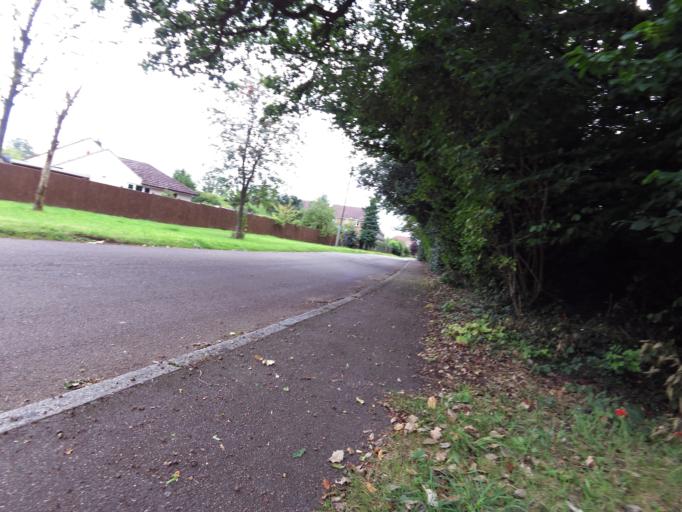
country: GB
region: England
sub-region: Hertfordshire
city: Hatfield
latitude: 51.7416
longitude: -0.2674
